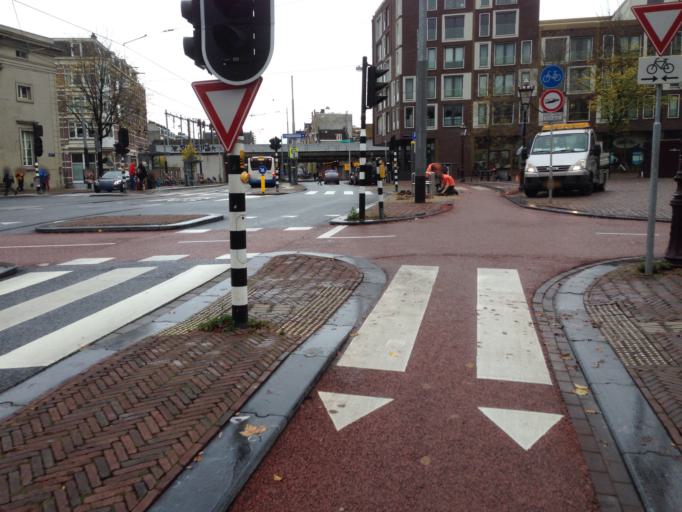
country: NL
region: North Holland
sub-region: Gemeente Amsterdam
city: Amsterdam
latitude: 52.3845
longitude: 4.8831
